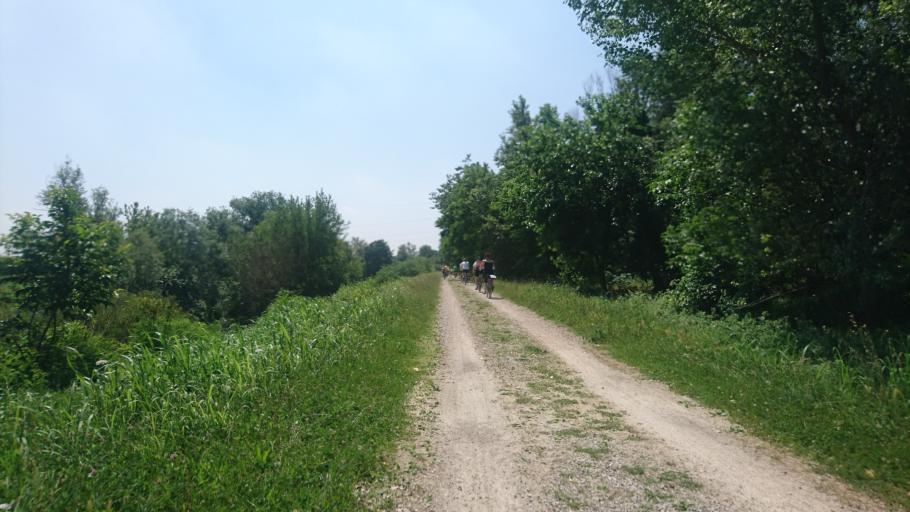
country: IT
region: Veneto
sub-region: Provincia di Venezia
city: Vigonovo
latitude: 45.3939
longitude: 12.0088
